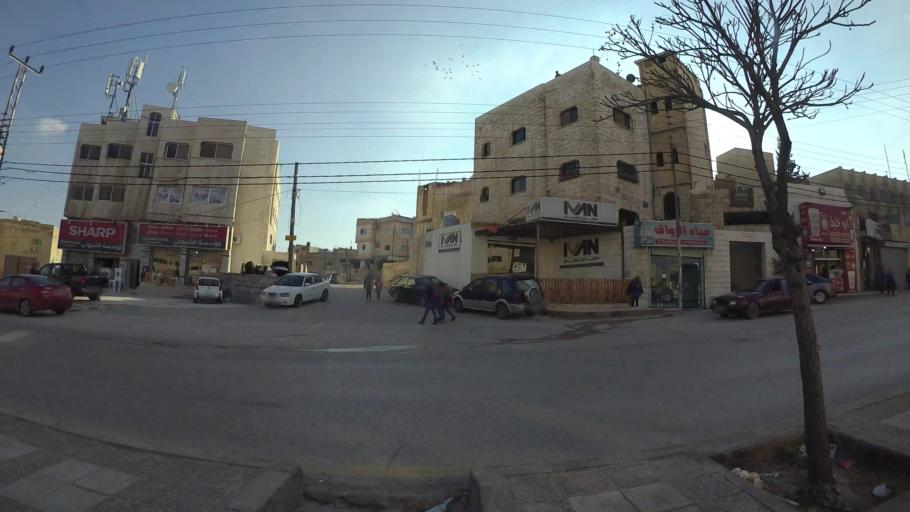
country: JO
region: Amman
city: Amman
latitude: 31.9772
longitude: 35.9445
